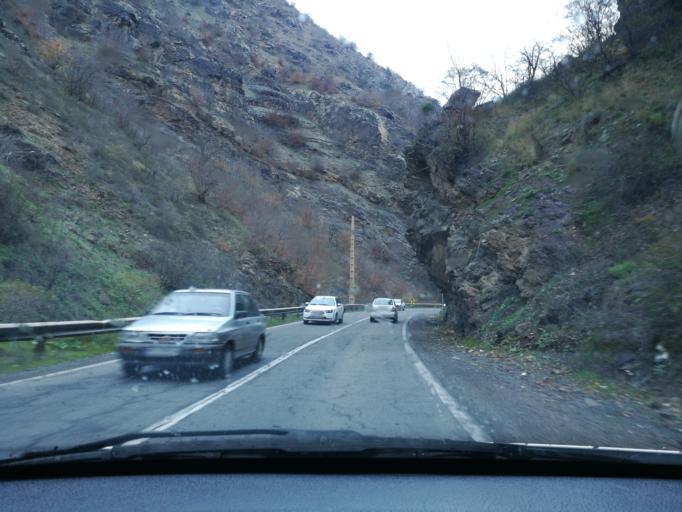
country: IR
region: Mazandaran
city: Chalus
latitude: 36.2832
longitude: 51.2422
